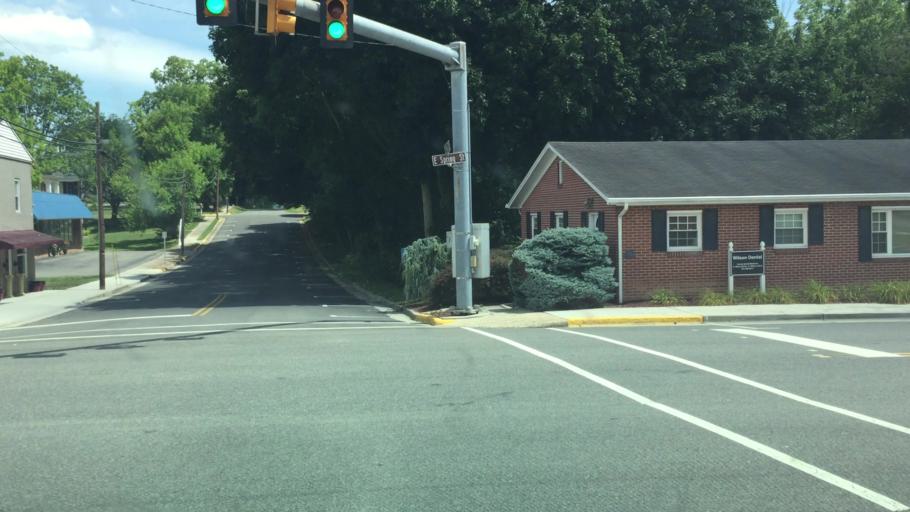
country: US
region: Virginia
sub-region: Wythe County
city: Wytheville
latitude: 36.9499
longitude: -81.0819
